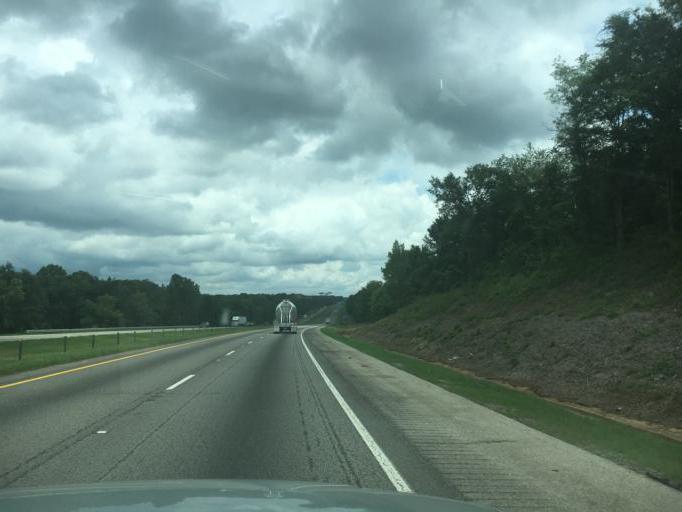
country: US
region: Georgia
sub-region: Banks County
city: Maysville
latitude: 34.2169
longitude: -83.5257
